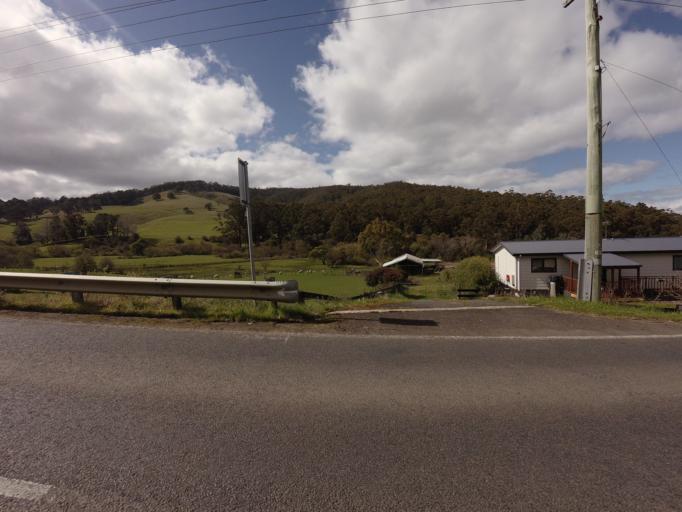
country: AU
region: Tasmania
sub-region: Huon Valley
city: Cygnet
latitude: -43.3107
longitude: 147.0140
